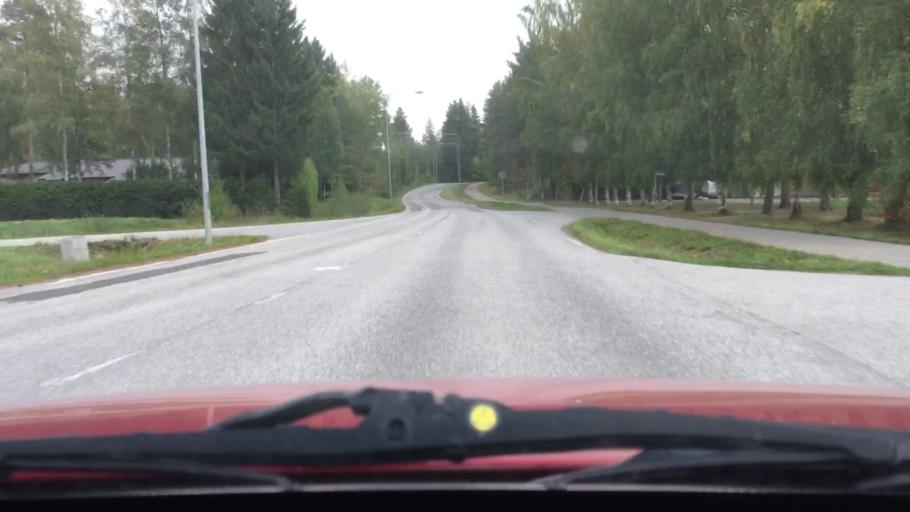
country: FI
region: Varsinais-Suomi
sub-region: Turku
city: Masku
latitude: 60.5556
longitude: 22.1284
